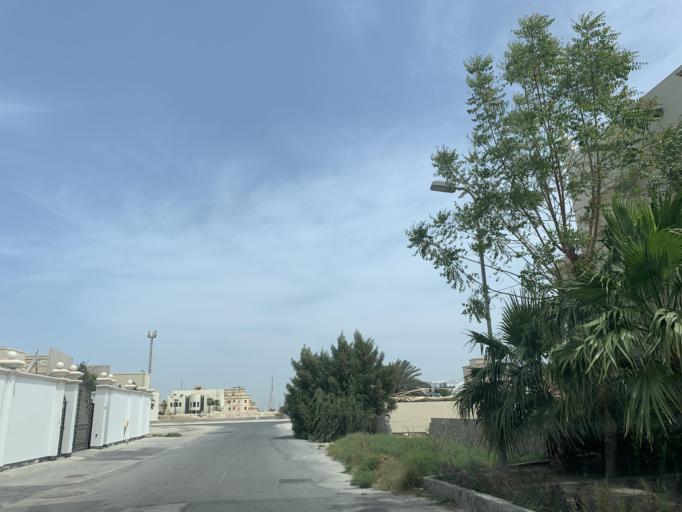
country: BH
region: Northern
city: Ar Rifa'
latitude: 26.1425
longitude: 50.5567
